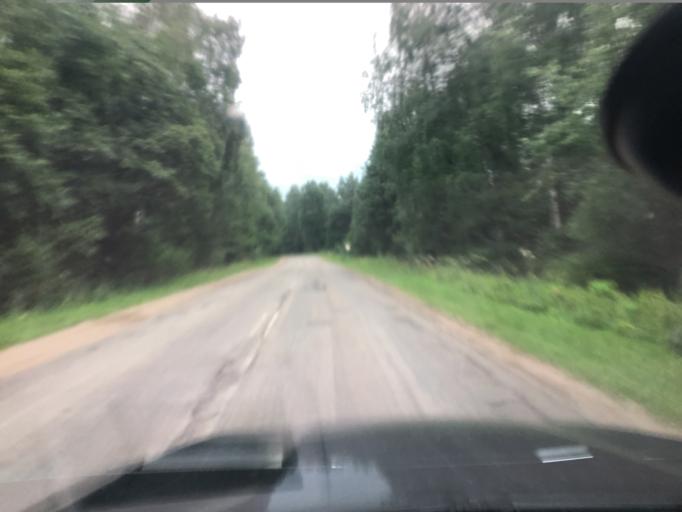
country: RU
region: Jaroslavl
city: Petrovsk
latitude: 56.9857
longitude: 39.2014
